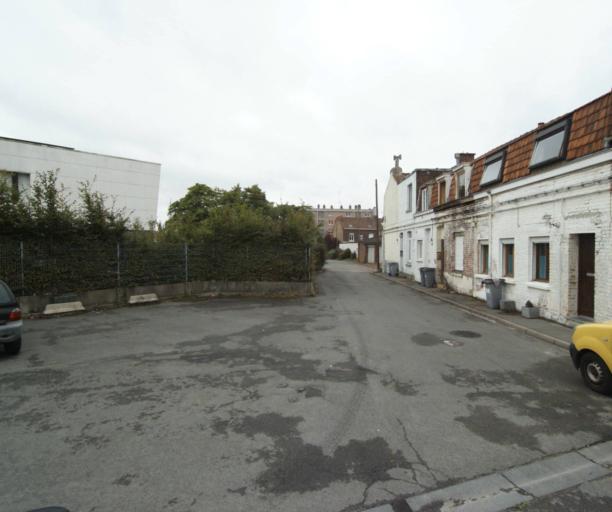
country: FR
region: Nord-Pas-de-Calais
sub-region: Departement du Nord
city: Ronchin
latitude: 50.6124
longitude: 3.0799
